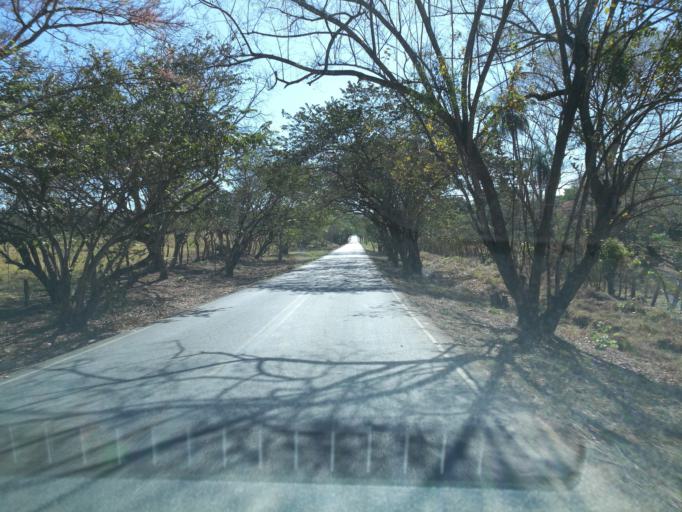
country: CR
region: Puntarenas
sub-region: Canton Central de Puntarenas
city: Puntarenas
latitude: 10.1101
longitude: -84.9146
